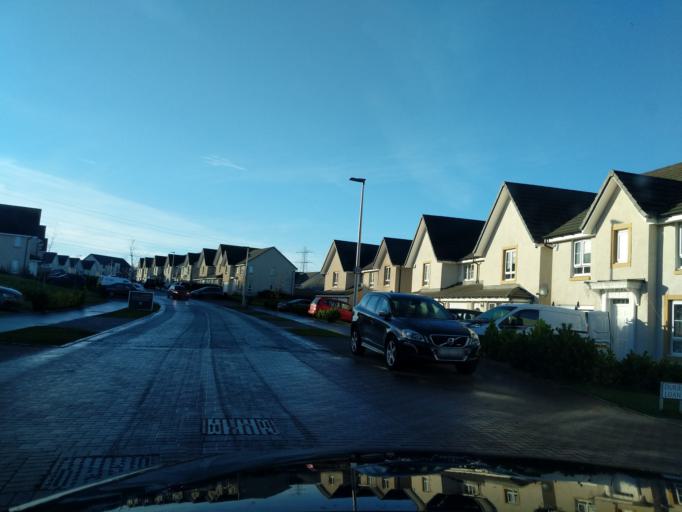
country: GB
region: Scotland
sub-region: Midlothian
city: Loanhead
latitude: 55.8940
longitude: -3.1575
